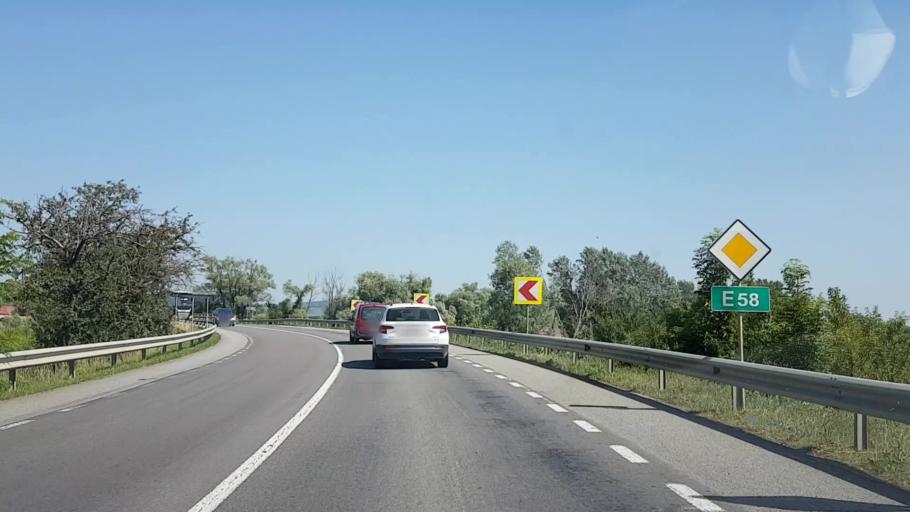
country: RO
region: Bistrita-Nasaud
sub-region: Comuna Sintereag
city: Sintereag
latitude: 47.1801
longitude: 24.2705
